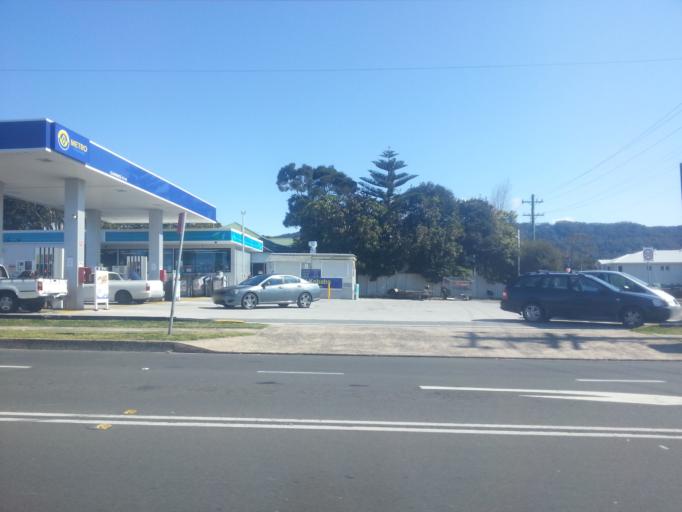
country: AU
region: New South Wales
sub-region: Wollongong
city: East Corrimal
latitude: -34.3686
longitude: 150.9103
